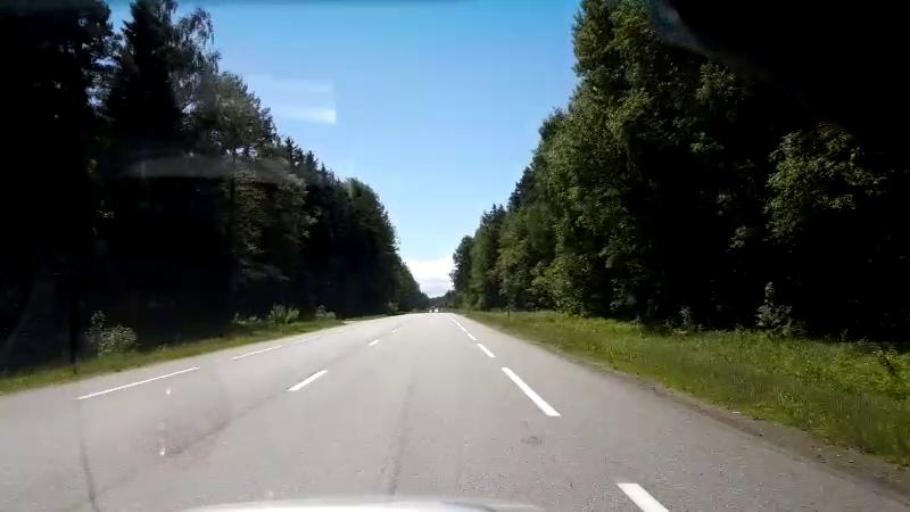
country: LV
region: Saulkrastu
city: Saulkrasti
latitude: 57.4299
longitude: 24.4295
